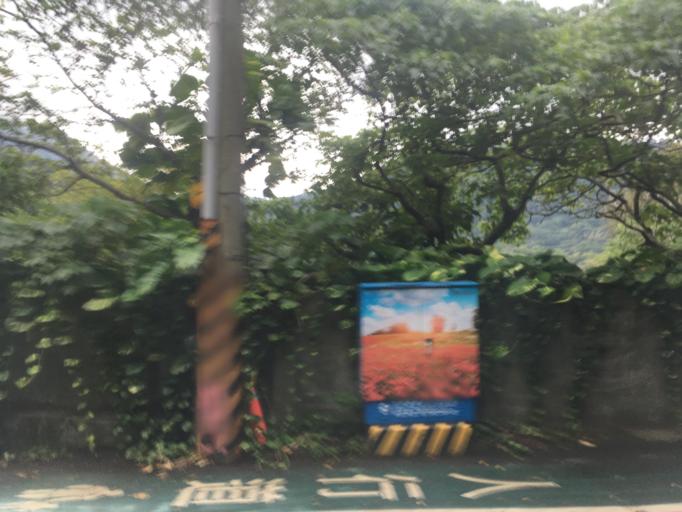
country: TW
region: Taipei
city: Taipei
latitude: 25.1406
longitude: 121.5278
